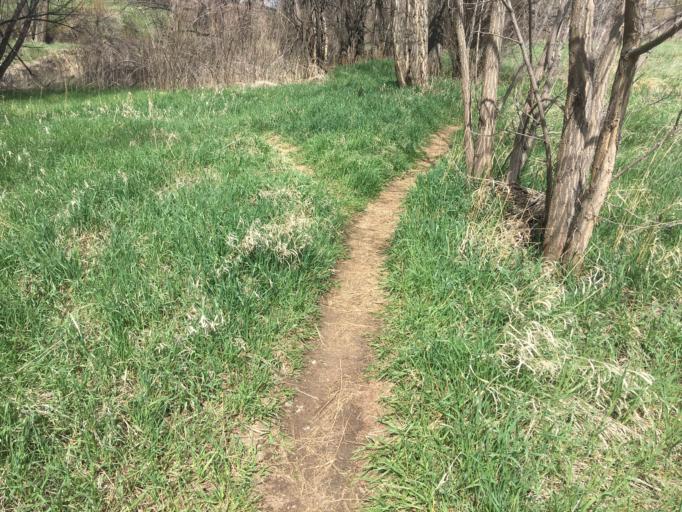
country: US
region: Colorado
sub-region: Boulder County
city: Gunbarrel
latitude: 40.0502
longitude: -105.1875
